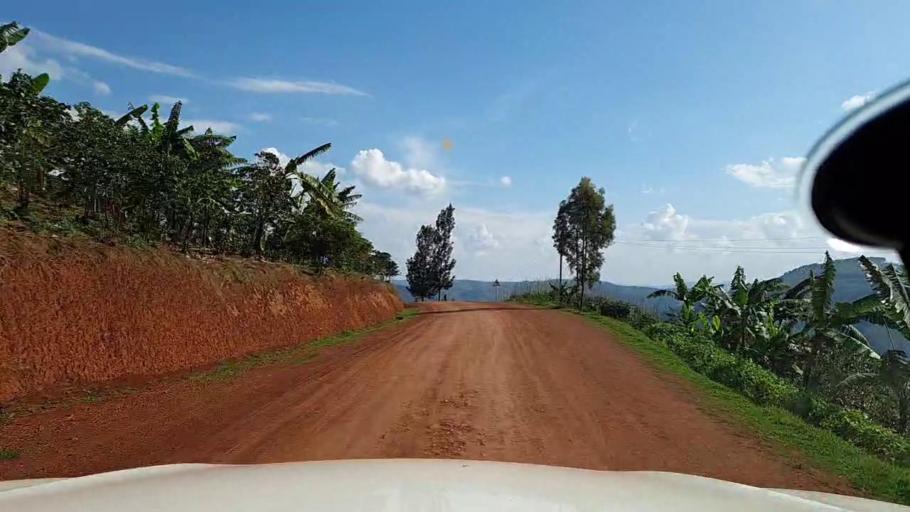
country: RW
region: Kigali
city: Kigali
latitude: -1.8355
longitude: 29.8464
